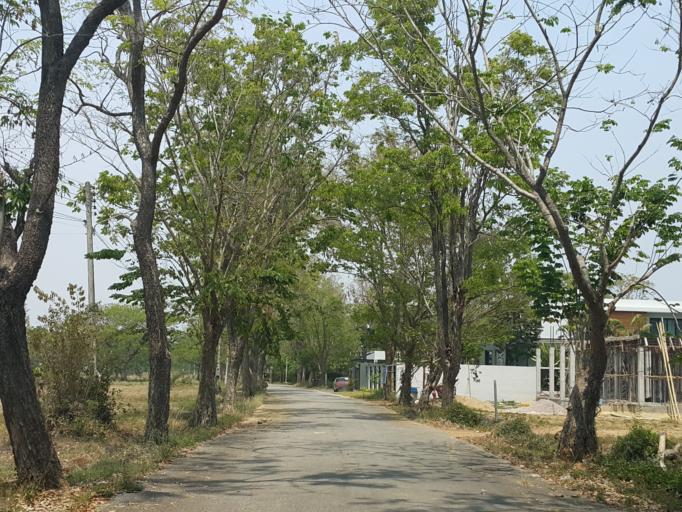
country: TH
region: Chiang Mai
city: Saraphi
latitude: 18.7274
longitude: 98.9792
